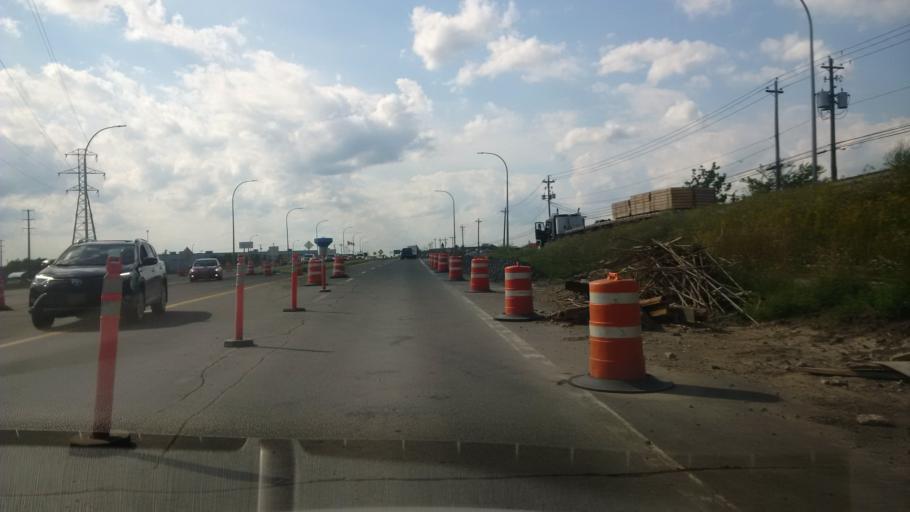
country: CA
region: New Brunswick
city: Fredericton
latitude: 45.9370
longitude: -66.6606
